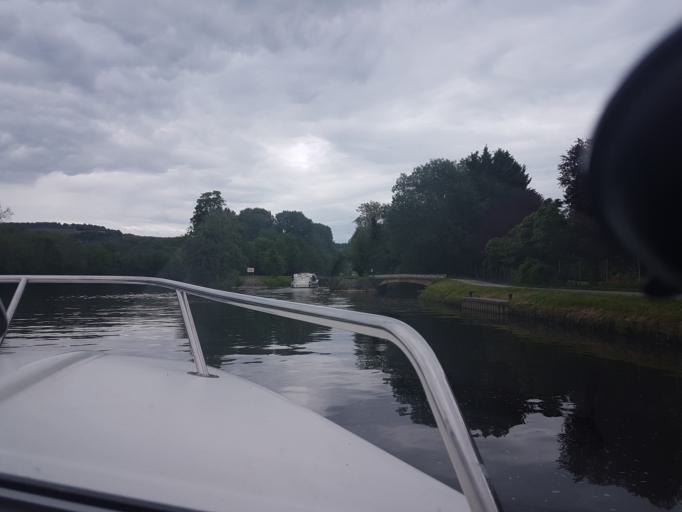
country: FR
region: Bourgogne
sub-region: Departement de l'Yonne
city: Champs-sur-Yonne
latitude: 47.7243
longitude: 3.6148
